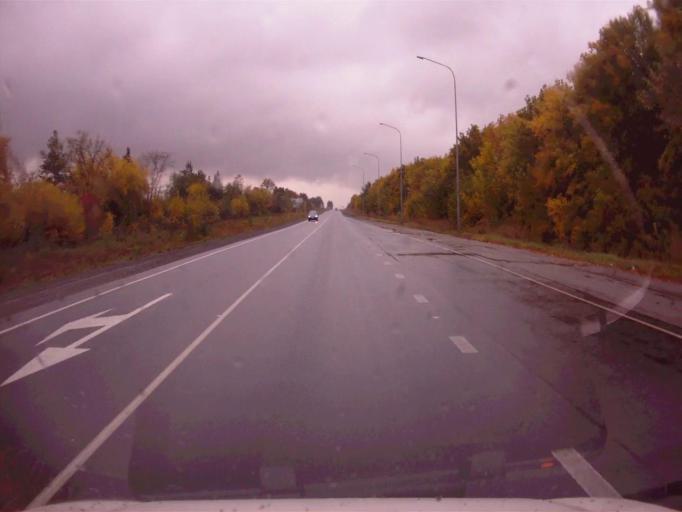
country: RU
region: Chelyabinsk
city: Roshchino
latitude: 55.3698
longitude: 61.1787
